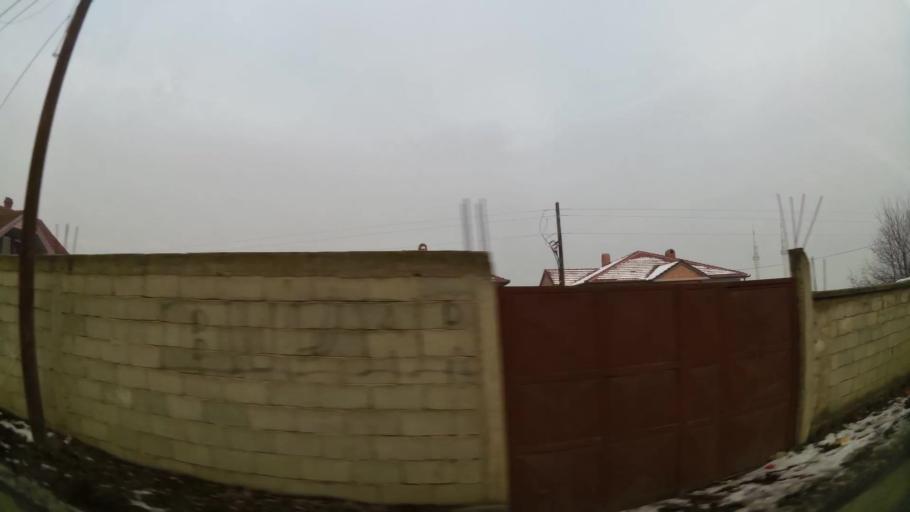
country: MK
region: Suto Orizari
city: Suto Orizare
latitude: 42.0335
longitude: 21.4159
